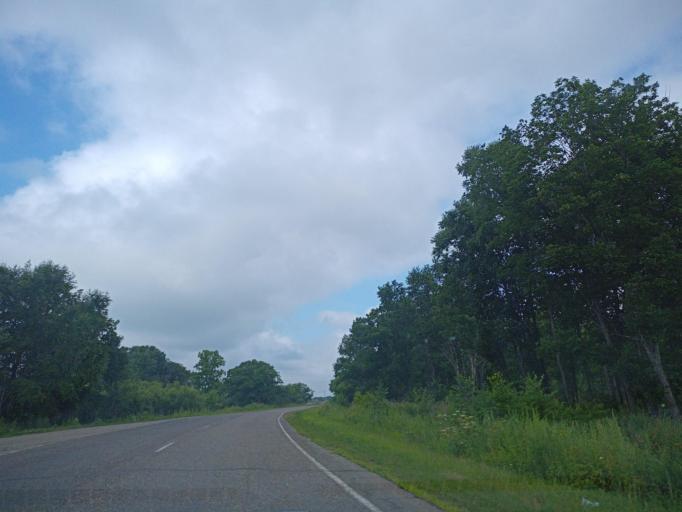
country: RU
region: Primorskiy
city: Dal'nerechensk
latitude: 45.9373
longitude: 133.8673
